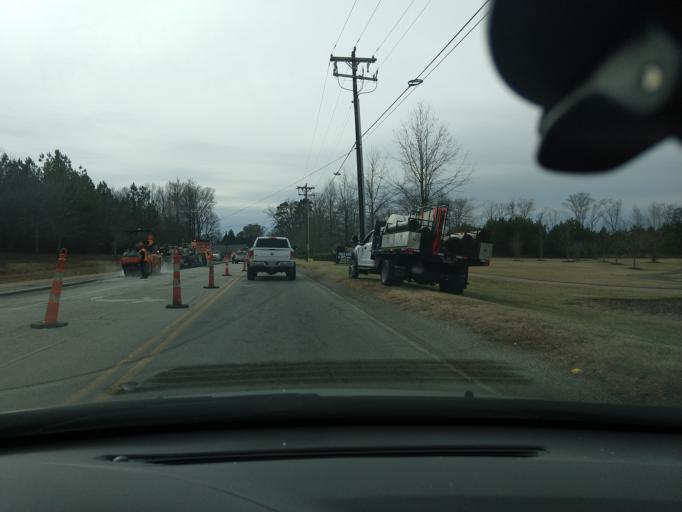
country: US
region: South Carolina
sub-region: Spartanburg County
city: Spartanburg
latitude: 34.9760
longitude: -81.8953
